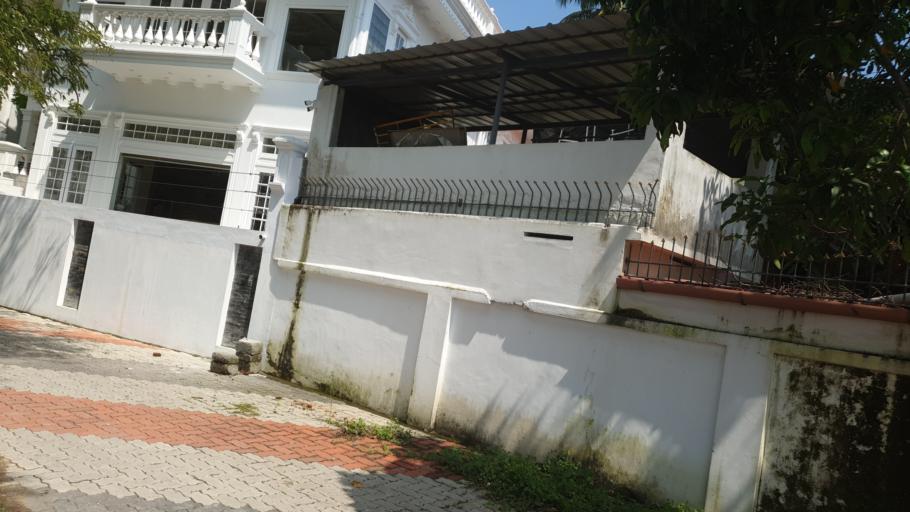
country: IN
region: Kerala
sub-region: Ernakulam
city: Cochin
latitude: 9.9726
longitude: 76.2417
